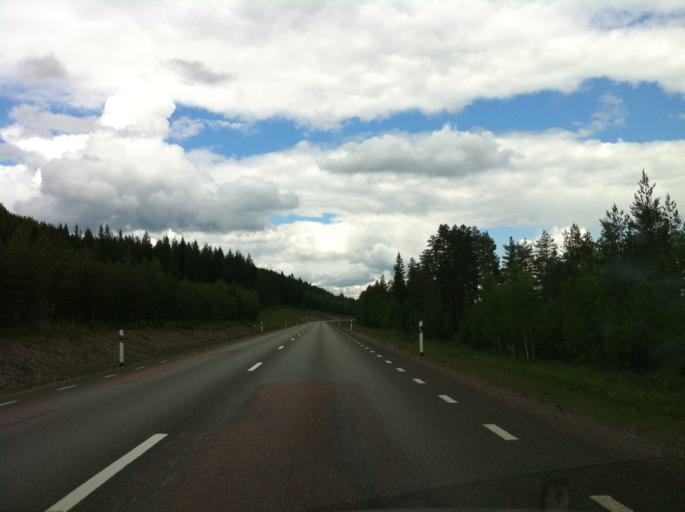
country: SE
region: Dalarna
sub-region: Malung-Saelens kommun
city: Malung
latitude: 60.6178
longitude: 13.6082
